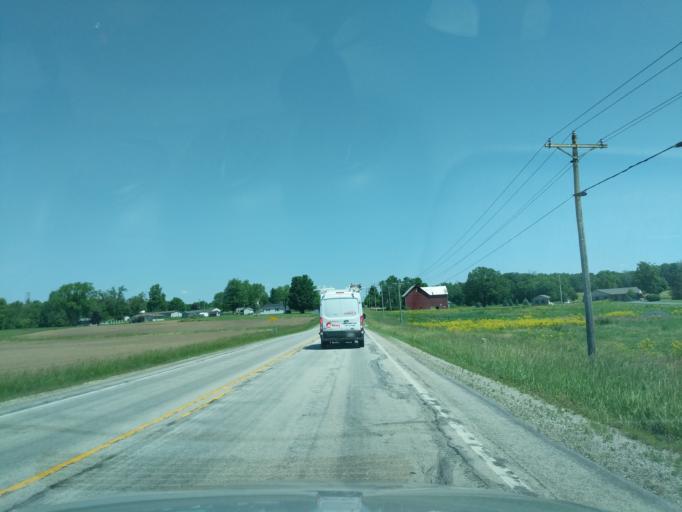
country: US
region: Indiana
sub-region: Whitley County
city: Columbia City
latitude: 41.1902
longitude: -85.4915
